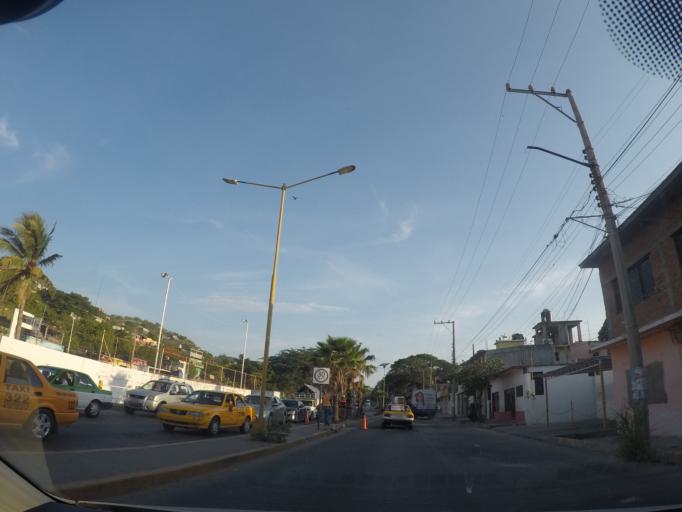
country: MX
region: Oaxaca
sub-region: Salina Cruz
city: Salina Cruz
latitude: 16.1857
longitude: -95.2002
